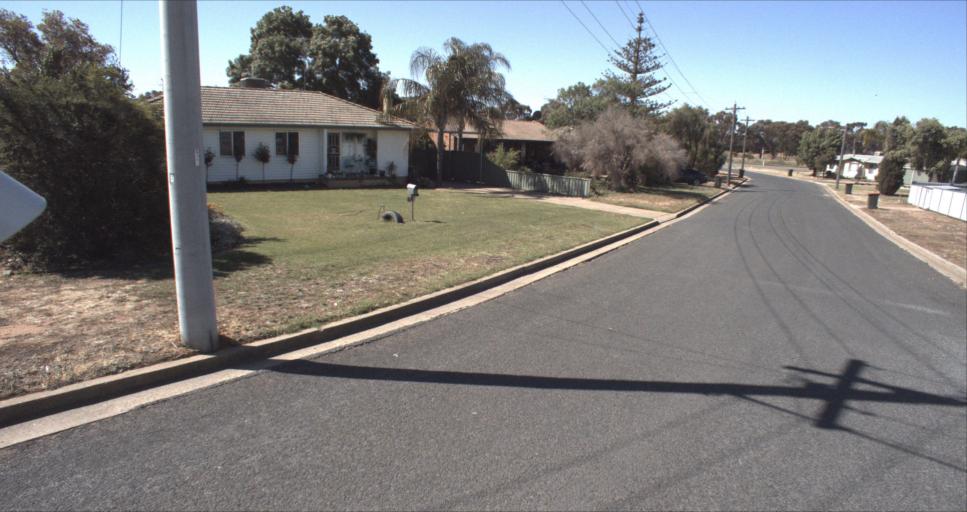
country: AU
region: New South Wales
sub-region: Leeton
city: Leeton
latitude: -34.5487
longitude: 146.3774
